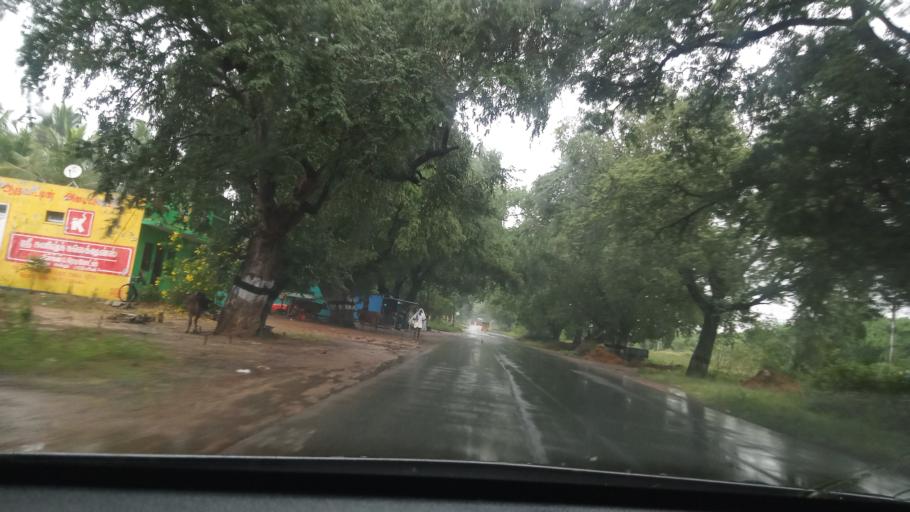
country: IN
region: Tamil Nadu
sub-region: Vellore
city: Walajapet
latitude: 12.8563
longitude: 79.3818
